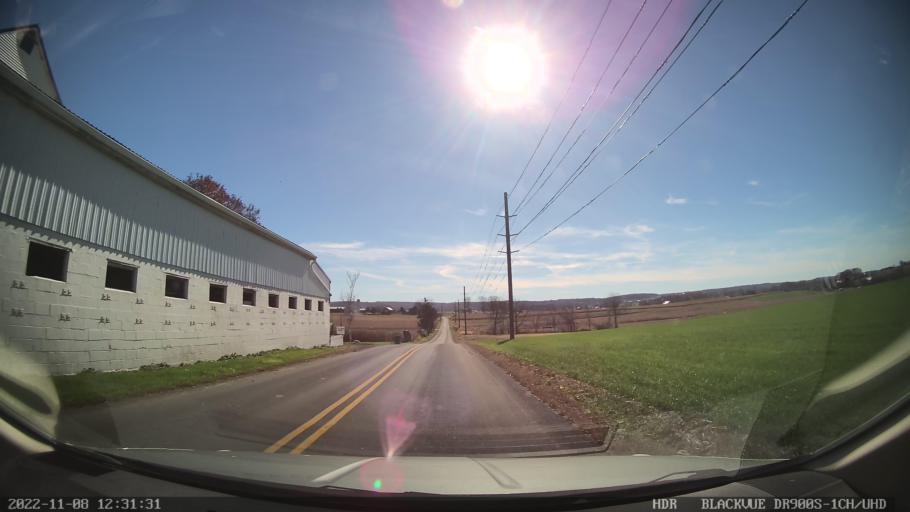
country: US
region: Pennsylvania
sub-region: Berks County
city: Kutztown
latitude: 40.5134
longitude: -75.7482
